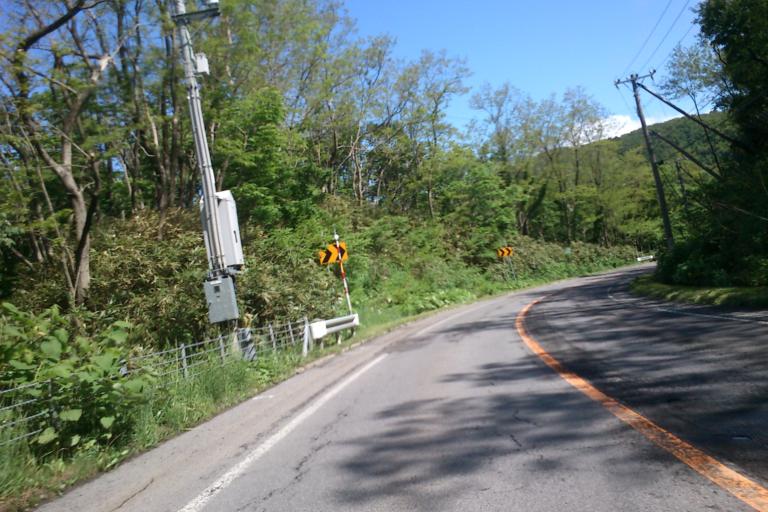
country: JP
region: Hokkaido
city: Ishikari
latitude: 43.5515
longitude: 141.3976
